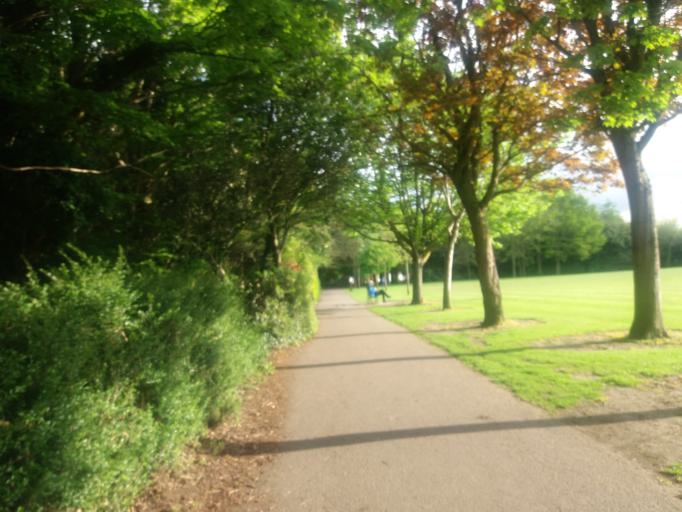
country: IE
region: Leinster
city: Glasnevin
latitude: 53.3828
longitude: -6.2622
